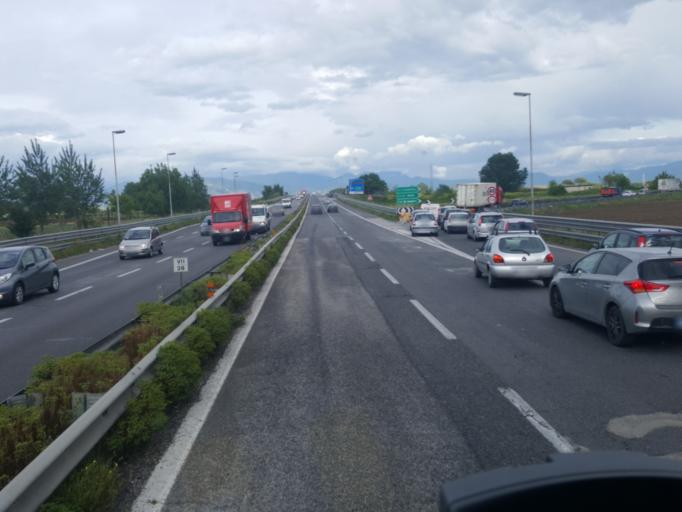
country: IT
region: Campania
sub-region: Provincia di Napoli
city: Pascarola
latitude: 40.9734
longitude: 14.3191
